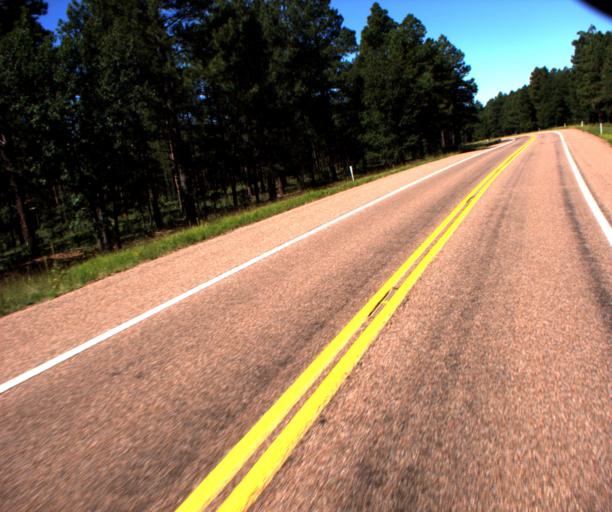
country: US
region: Arizona
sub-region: Navajo County
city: Pinetop-Lakeside
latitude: 34.0771
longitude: -109.8245
